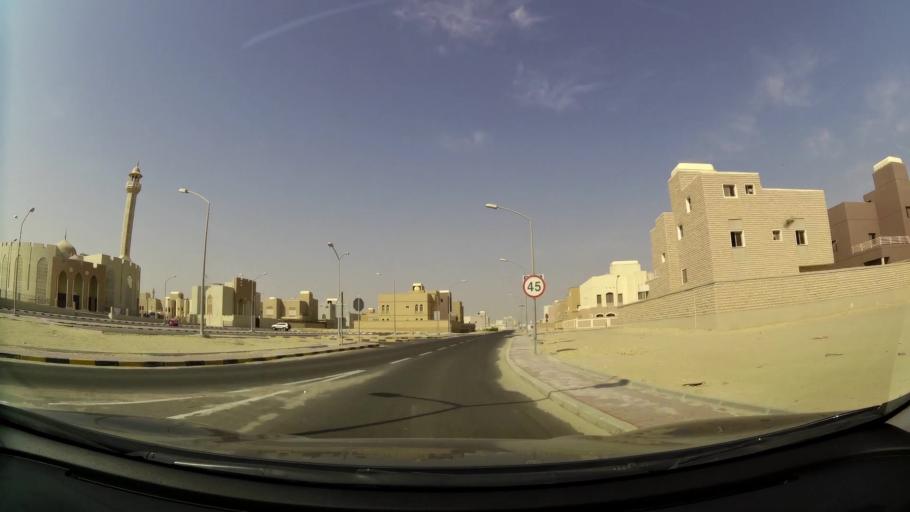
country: KW
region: Al Ahmadi
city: Al Wafrah
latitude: 28.8019
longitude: 48.0722
